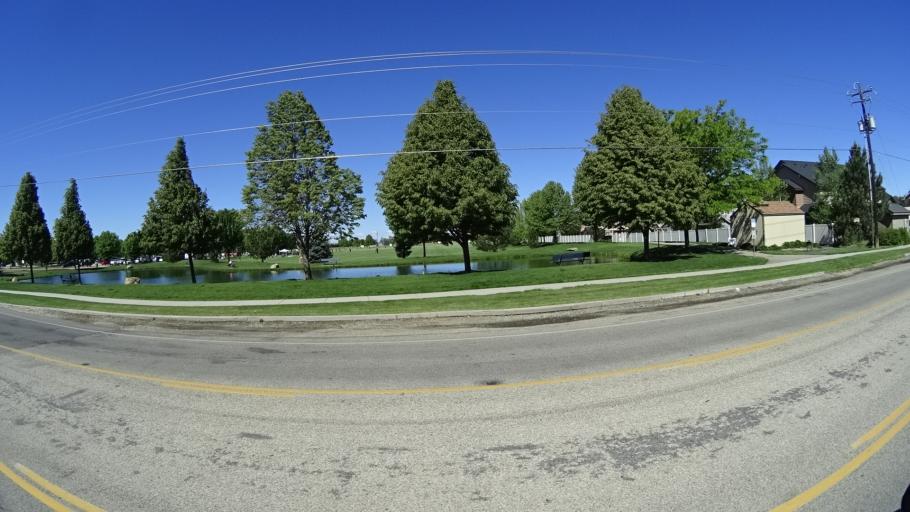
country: US
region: Idaho
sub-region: Ada County
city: Meridian
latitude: 43.6364
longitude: -116.3936
